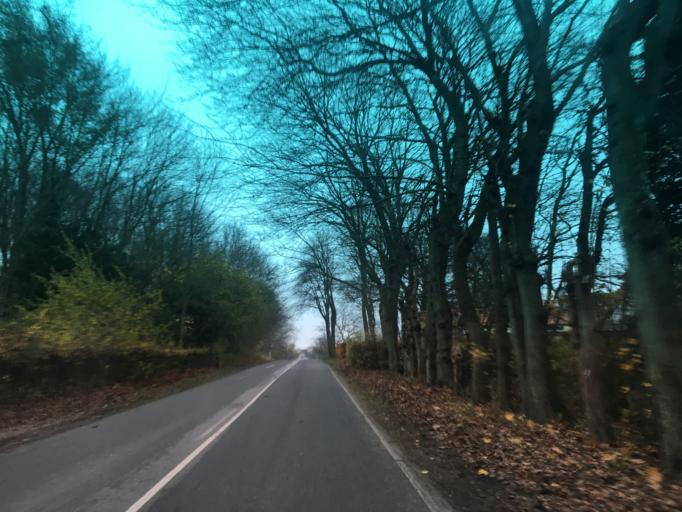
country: DK
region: Zealand
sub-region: Slagelse Kommune
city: Skaelskor
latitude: 55.2509
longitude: 11.4203
